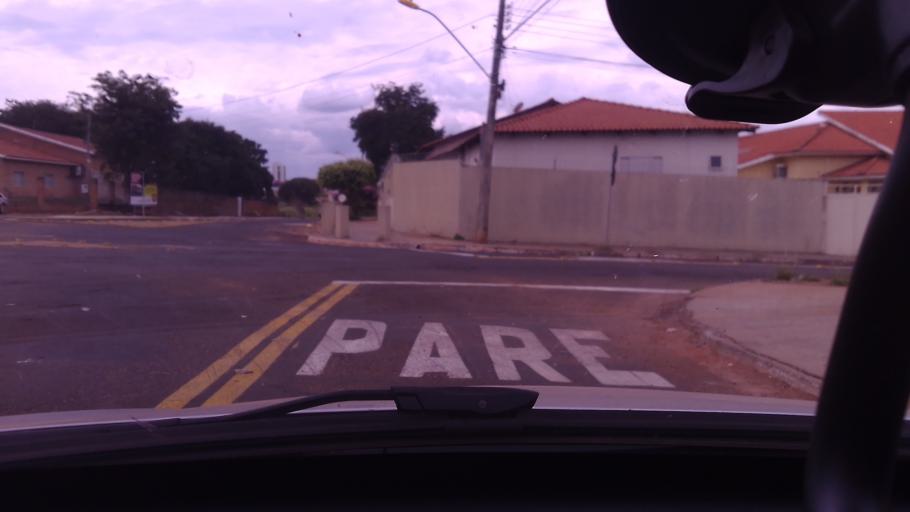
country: BR
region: Goias
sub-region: Mineiros
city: Mineiros
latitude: -17.5683
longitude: -52.5665
